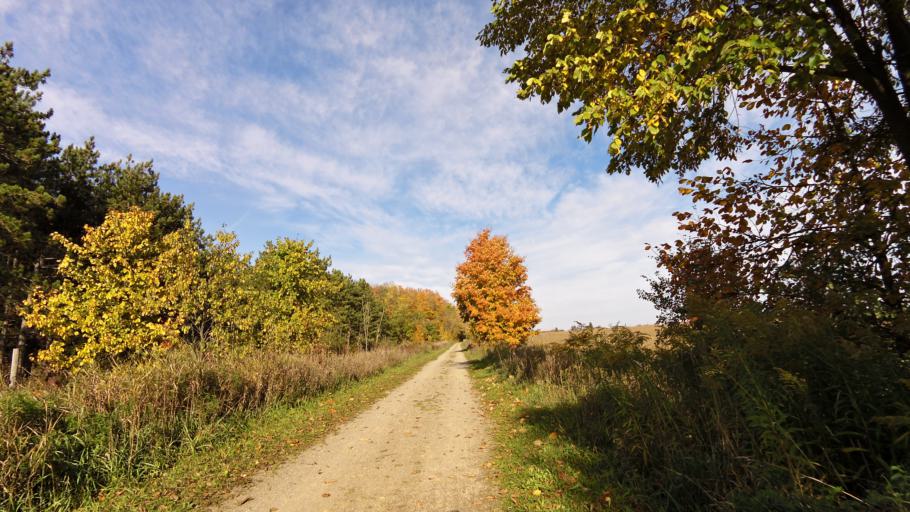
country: CA
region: Ontario
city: Orangeville
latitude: 43.7963
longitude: -80.0434
